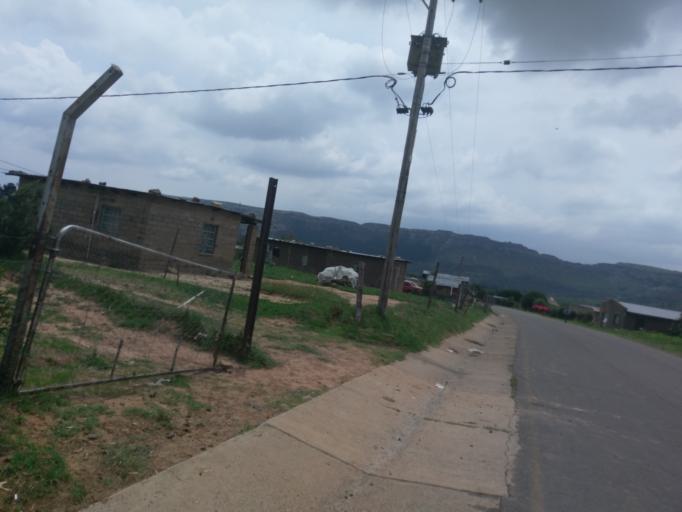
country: LS
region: Leribe
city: Leribe
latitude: -29.0295
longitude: 28.0244
